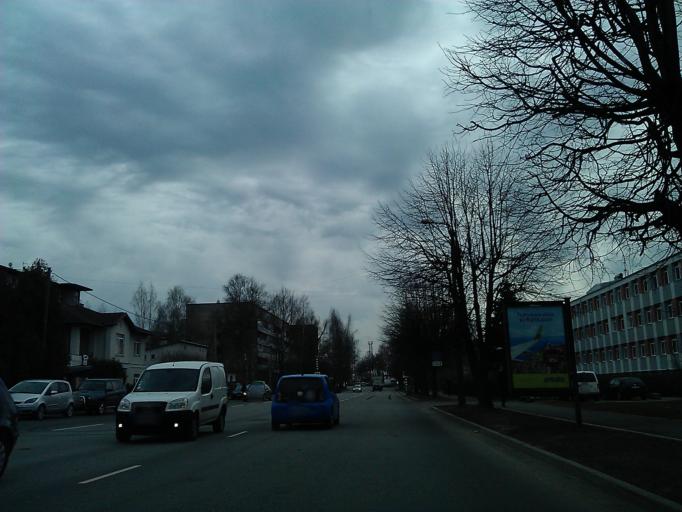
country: LV
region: Riga
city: Riga
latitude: 56.9644
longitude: 24.1653
